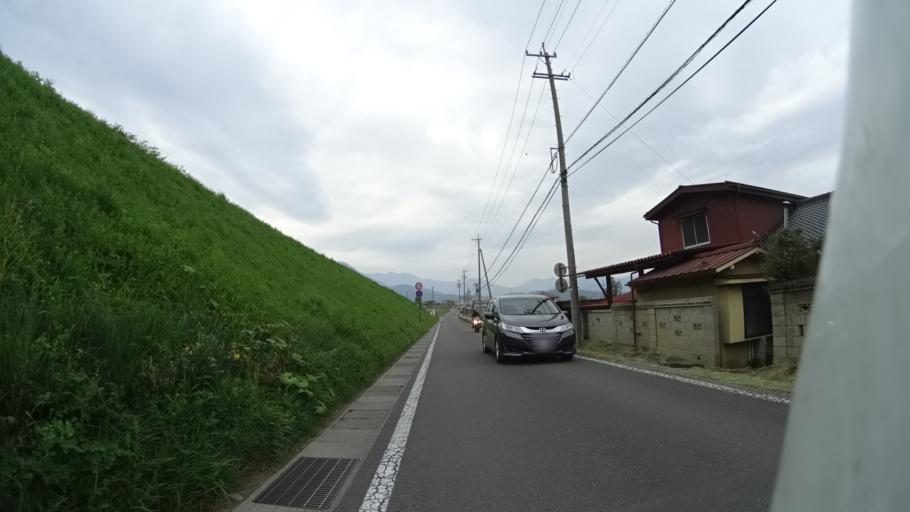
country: JP
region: Nagano
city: Kamimaruko
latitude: 36.3487
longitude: 138.2019
